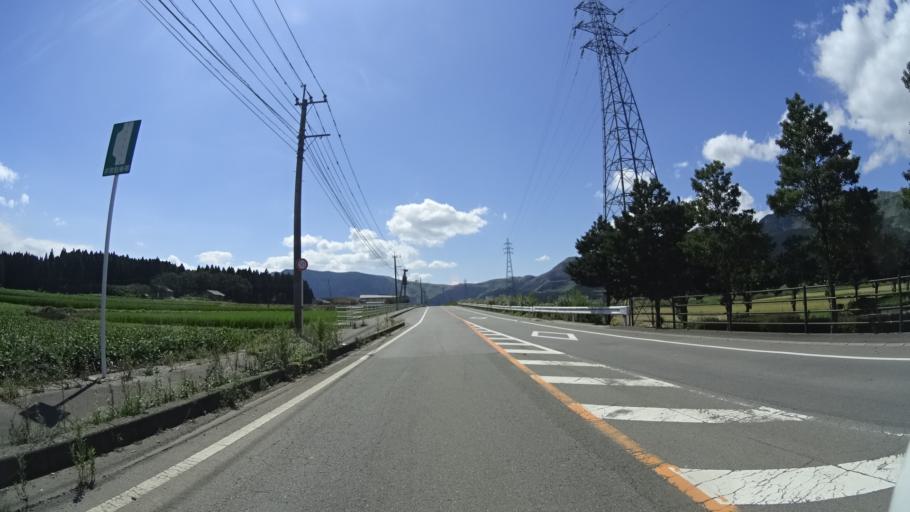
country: JP
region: Kumamoto
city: Aso
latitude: 32.9303
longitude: 131.0055
